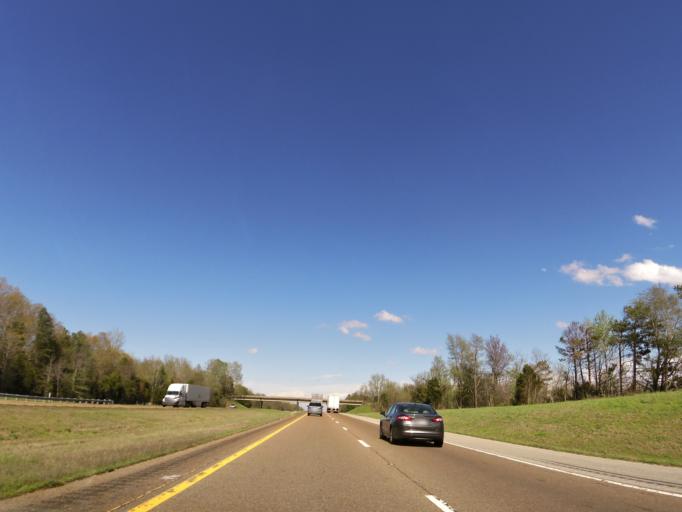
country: US
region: Tennessee
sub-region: Gibson County
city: Medina
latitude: 35.7354
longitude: -88.5865
